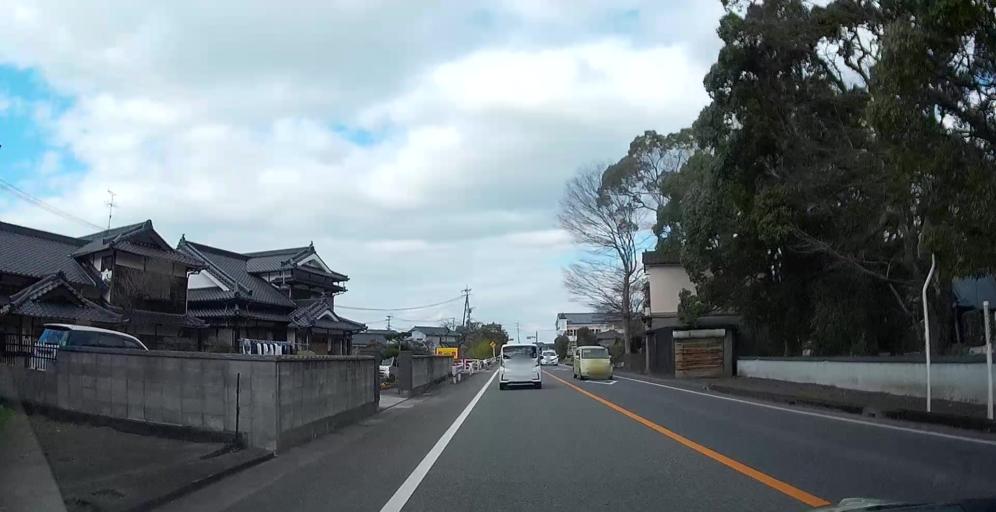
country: JP
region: Kumamoto
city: Yatsushiro
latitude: 32.4448
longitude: 130.5866
